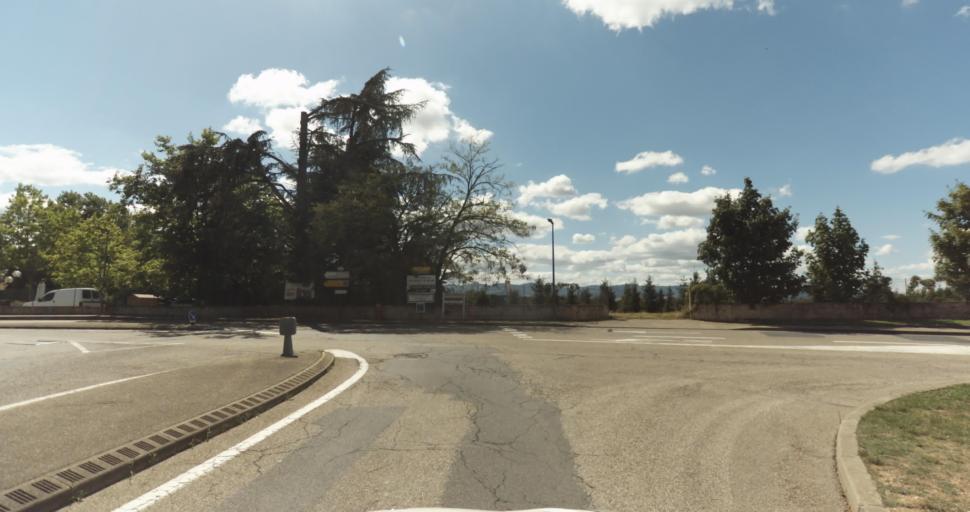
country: FR
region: Rhone-Alpes
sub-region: Departement du Rhone
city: Chaponost
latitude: 45.7209
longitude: 4.7599
